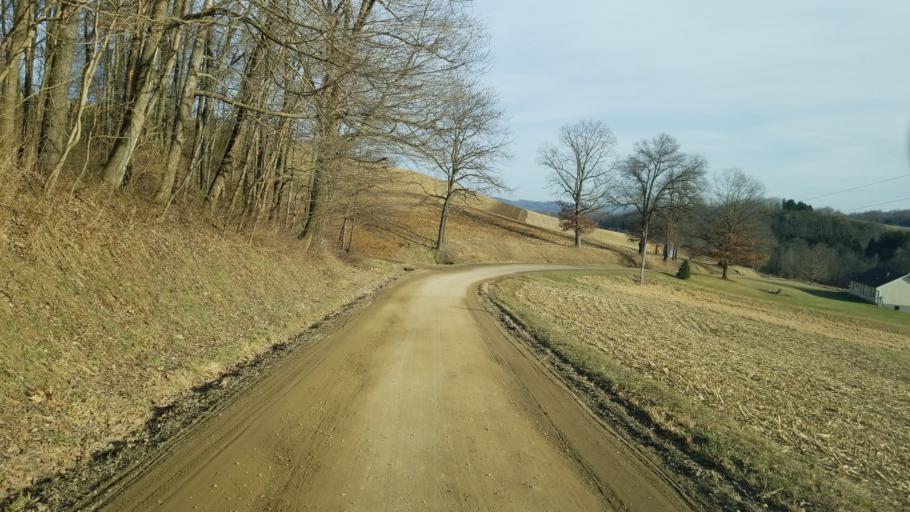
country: US
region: Pennsylvania
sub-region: Indiana County
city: Chevy Chase Heights
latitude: 40.8243
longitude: -79.1615
